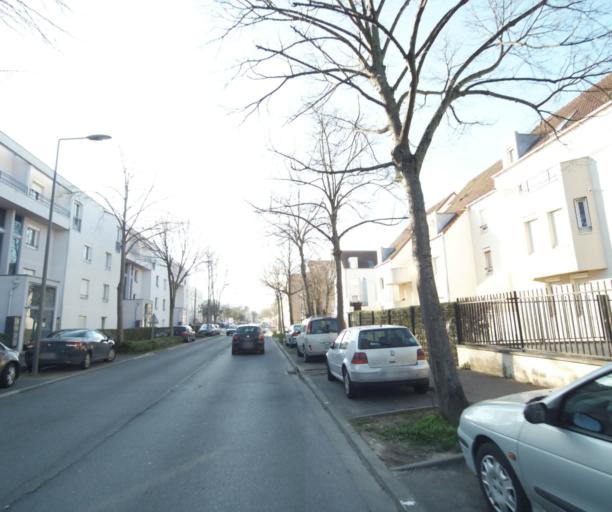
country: FR
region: Ile-de-France
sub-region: Departement du Val-d'Oise
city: Vaureal
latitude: 49.0467
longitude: 2.0360
